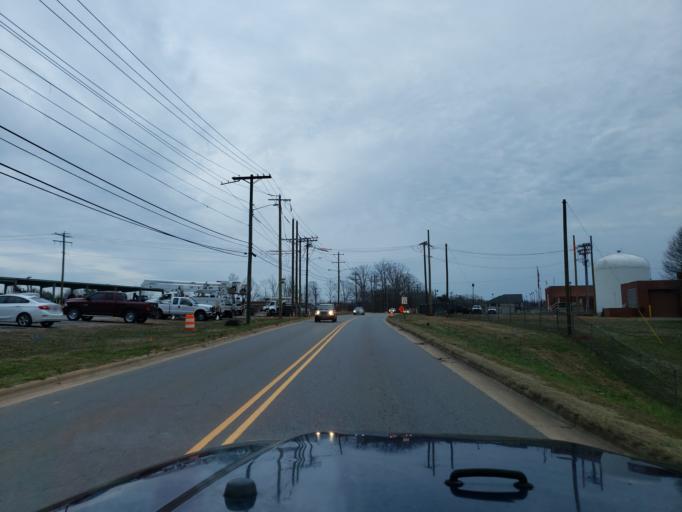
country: US
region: North Carolina
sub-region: Cleveland County
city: Shelby
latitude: 35.3041
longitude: -81.5581
